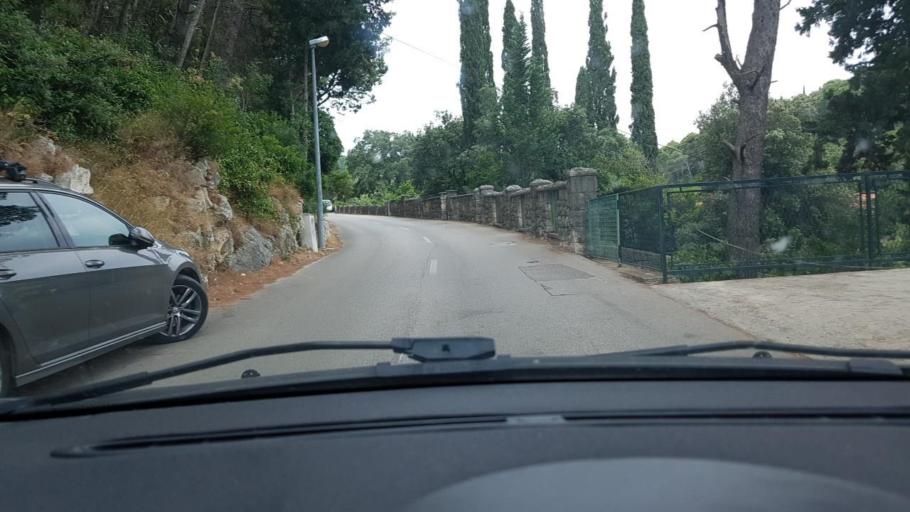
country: HR
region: Dubrovacko-Neretvanska
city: Korcula
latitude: 42.9615
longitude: 17.1278
